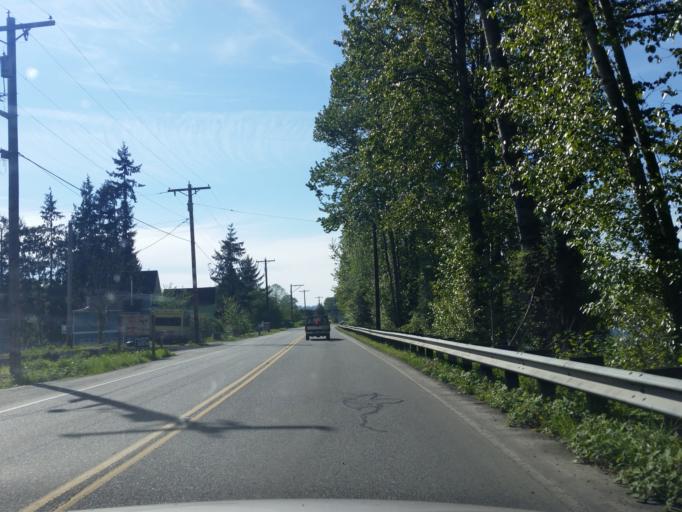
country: US
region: Washington
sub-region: Snohomish County
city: Snohomish
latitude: 47.9108
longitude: -122.1018
